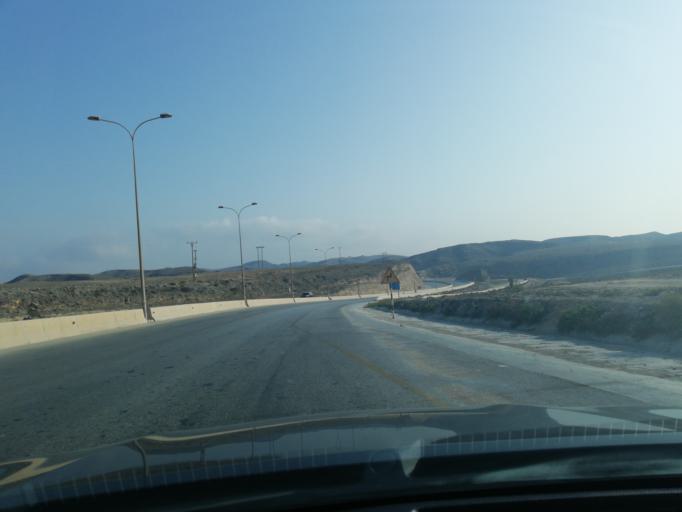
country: OM
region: Zufar
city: Salalah
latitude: 17.2776
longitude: 54.0854
